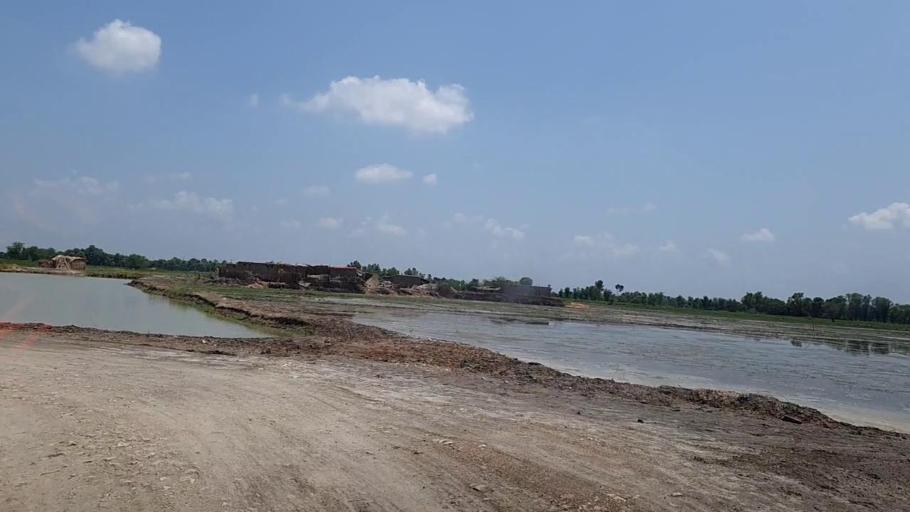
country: PK
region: Sindh
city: Kandiaro
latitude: 26.9856
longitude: 68.2347
